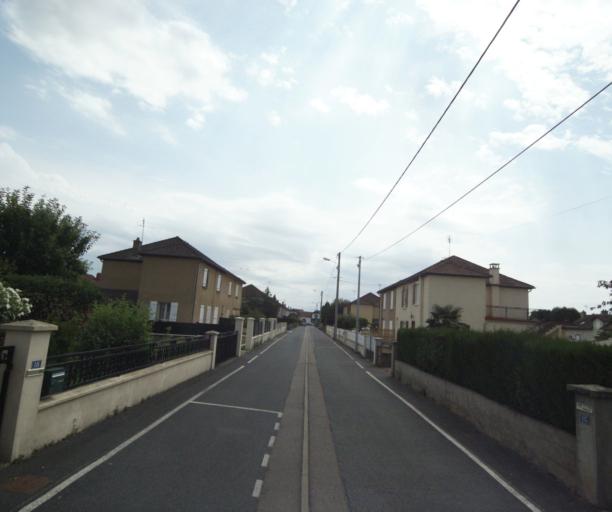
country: FR
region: Bourgogne
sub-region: Departement de Saone-et-Loire
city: Gueugnon
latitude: 46.6075
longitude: 4.0513
